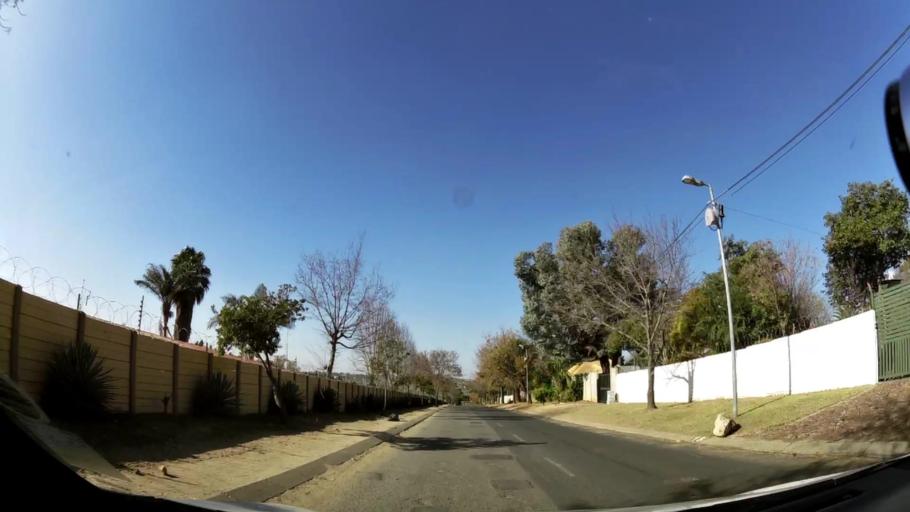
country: ZA
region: Gauteng
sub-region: City of Johannesburg Metropolitan Municipality
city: Diepsloot
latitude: -26.0230
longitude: 27.9685
